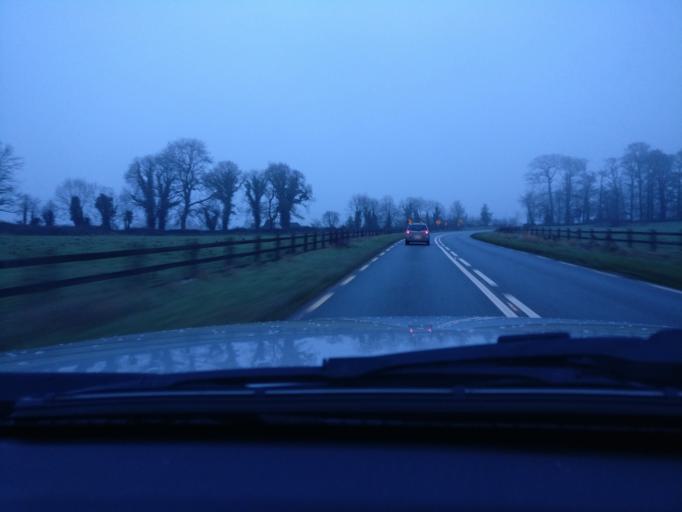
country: IE
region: Leinster
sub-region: An Mhi
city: Athboy
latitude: 53.6453
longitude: -6.8741
